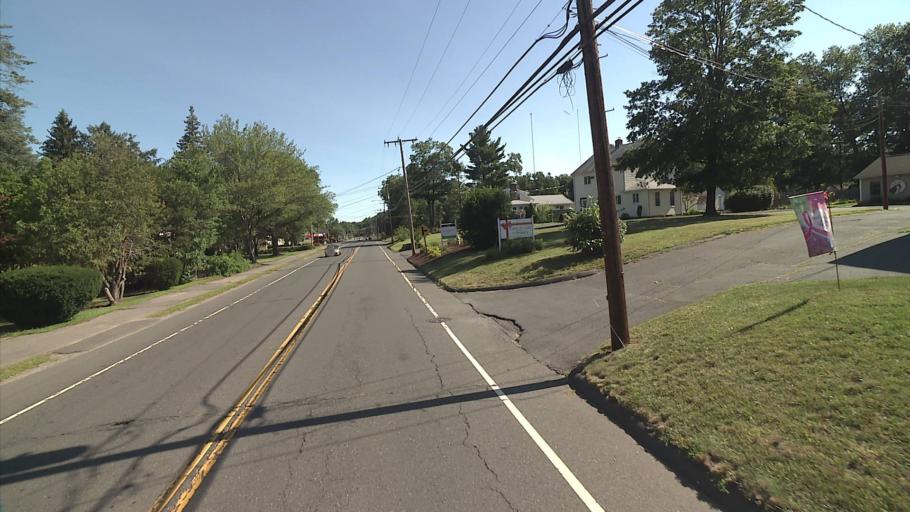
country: US
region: Connecticut
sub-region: Hartford County
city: Plainville
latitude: 41.6889
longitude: -72.8512
